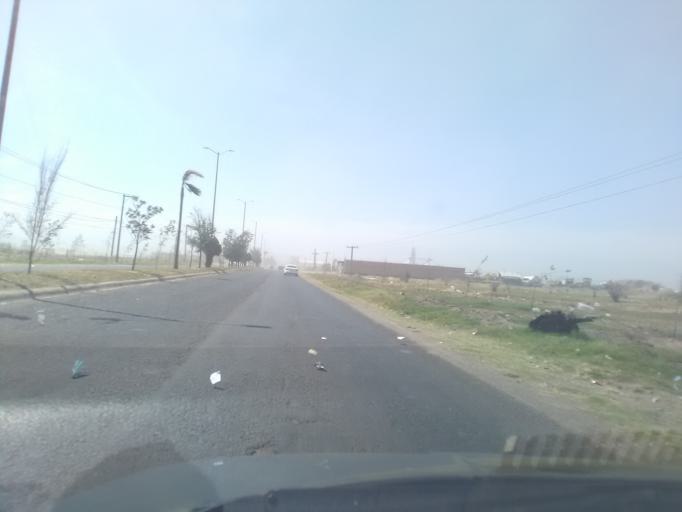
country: MX
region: Durango
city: Victoria de Durango
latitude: 24.0288
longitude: -104.5970
